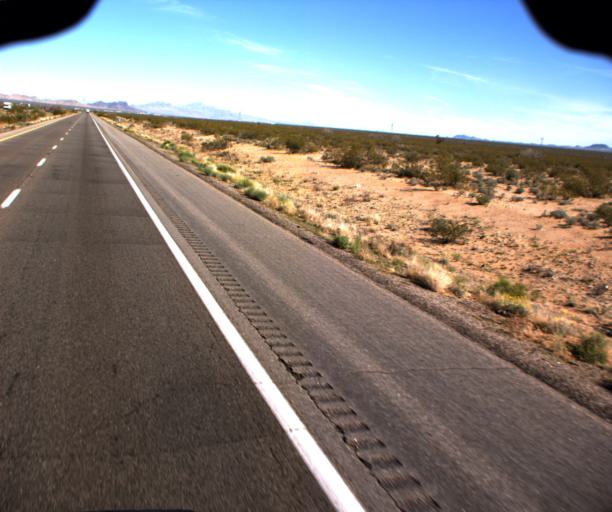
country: US
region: Arizona
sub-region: Mohave County
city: Dolan Springs
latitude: 35.6549
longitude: -114.4447
